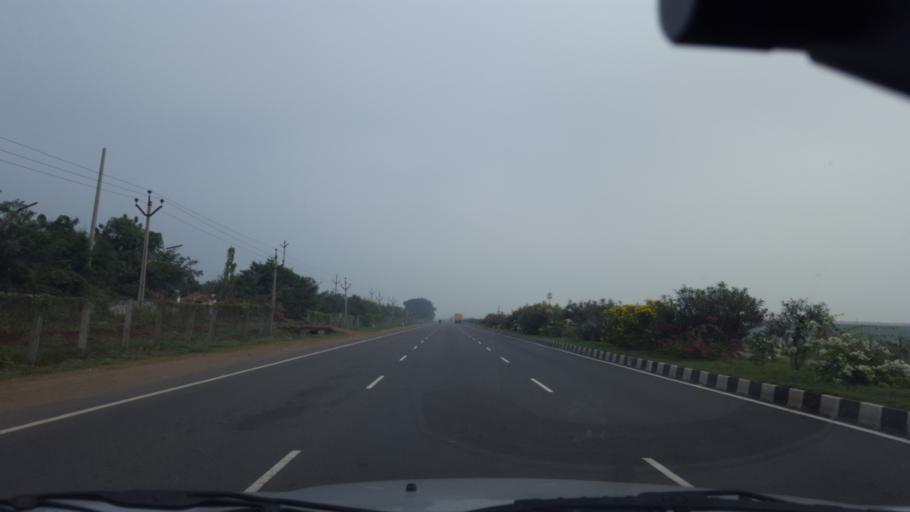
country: IN
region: Andhra Pradesh
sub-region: Prakasam
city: Addanki
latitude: 15.6671
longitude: 80.0157
